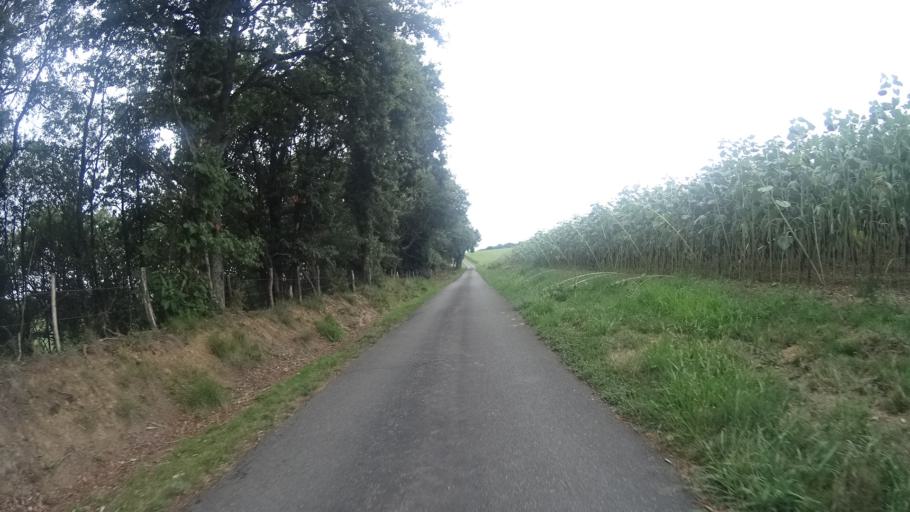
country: FR
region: Aquitaine
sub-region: Departement des Pyrenees-Atlantiques
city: Orthez
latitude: 43.4981
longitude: -0.6970
